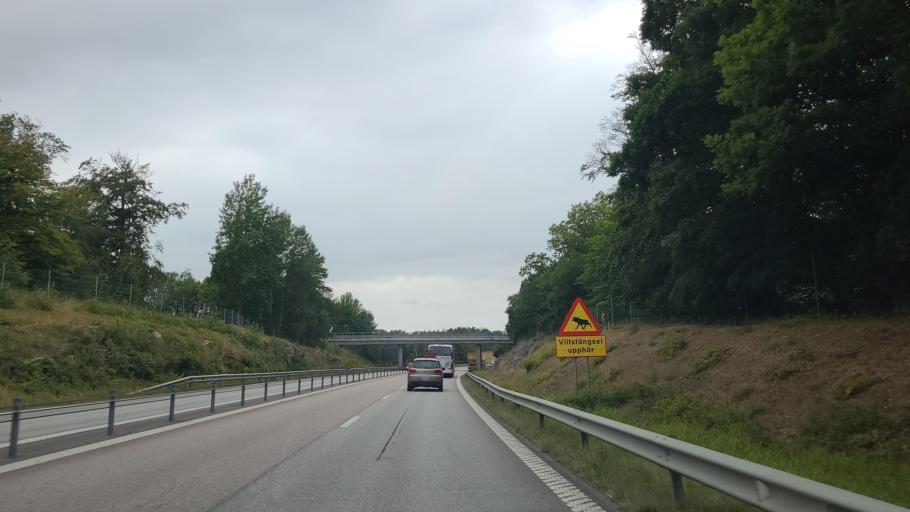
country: SE
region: Blekinge
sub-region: Karlshamns Kommun
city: Morrum
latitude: 56.1776
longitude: 14.7556
